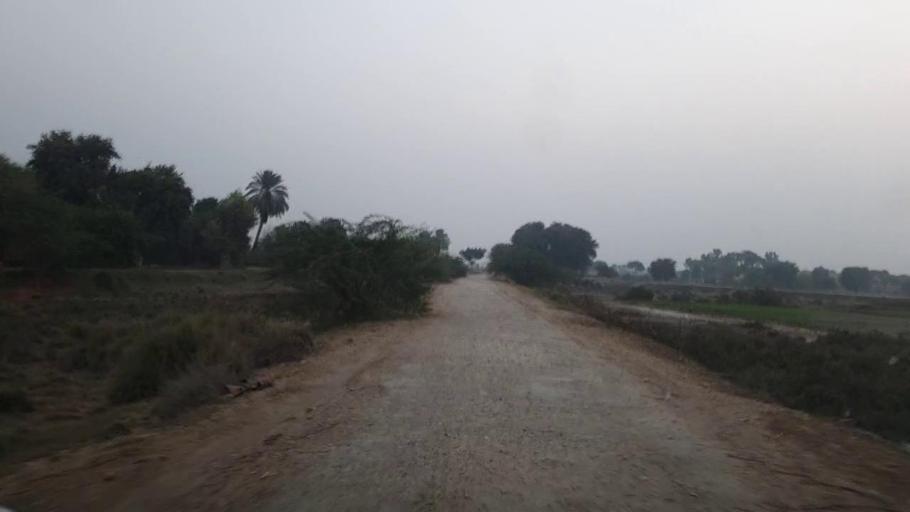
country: PK
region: Sindh
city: Karaundi
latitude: 26.9418
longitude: 68.4457
